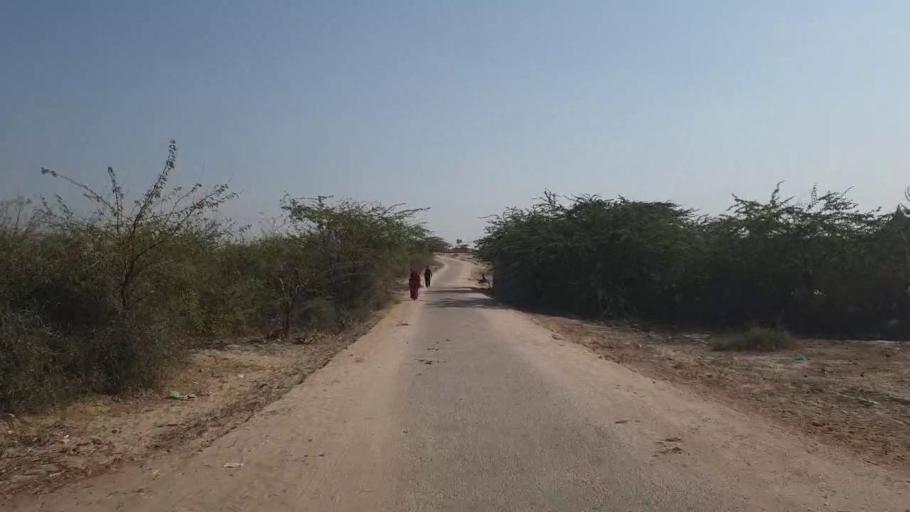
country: PK
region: Sindh
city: Dhoro Naro
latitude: 25.5022
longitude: 69.6301
